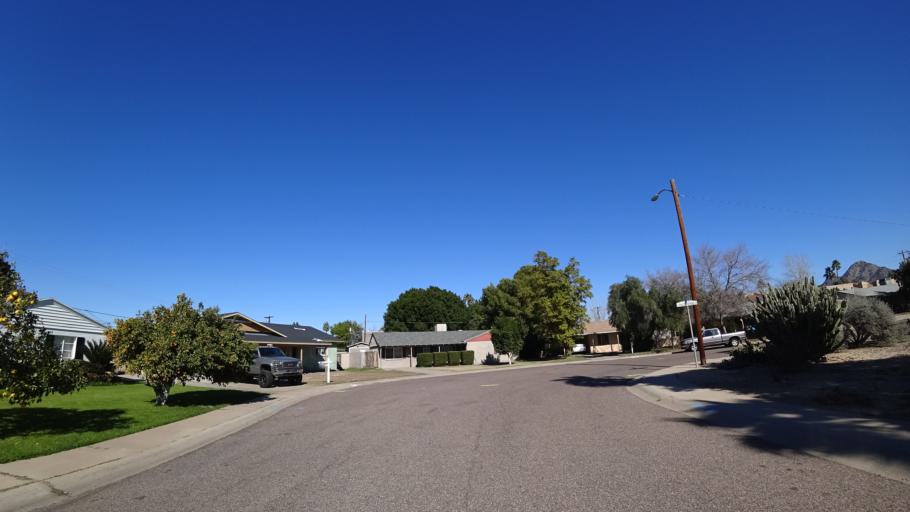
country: US
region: Arizona
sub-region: Maricopa County
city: Phoenix
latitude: 33.5221
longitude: -112.0580
